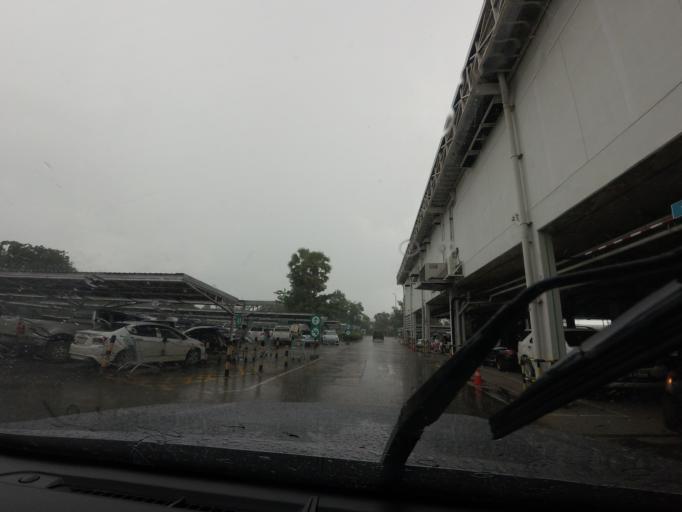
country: TH
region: Chumphon
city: Chumphon
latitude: 10.5042
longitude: 99.1389
